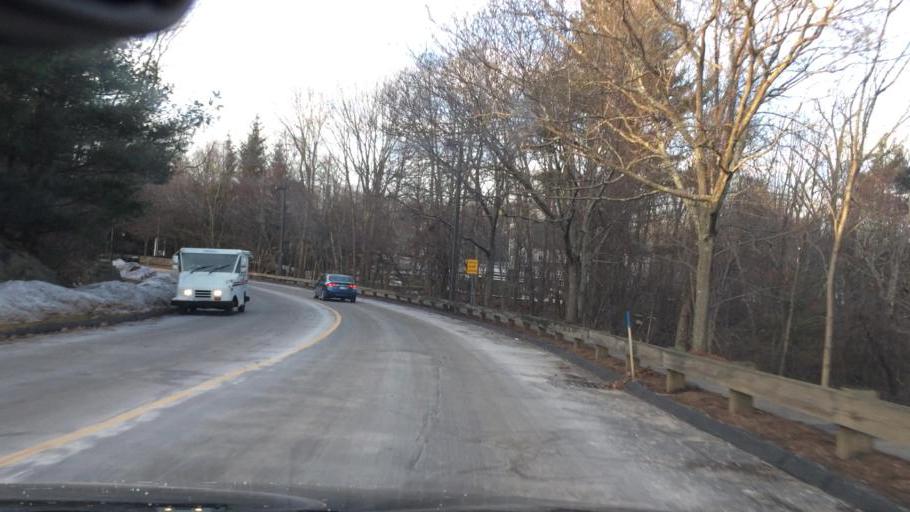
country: US
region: Massachusetts
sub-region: Middlesex County
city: Burlington
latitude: 42.4954
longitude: -71.1906
